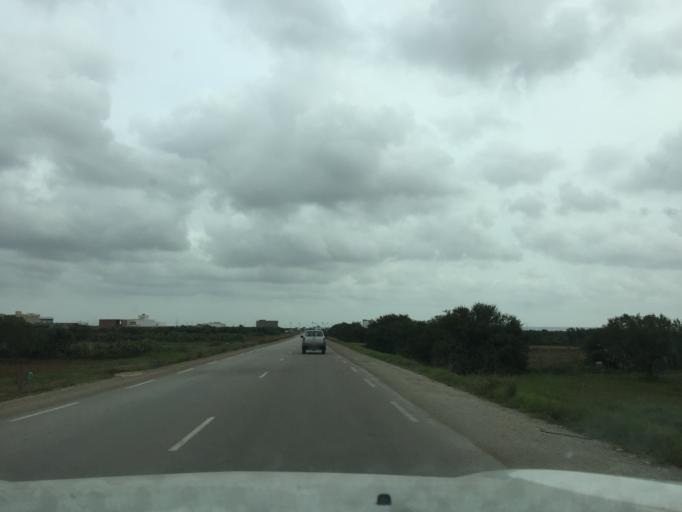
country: TN
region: Al Munastir
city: Manzil Kamil
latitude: 35.6193
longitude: 10.6791
